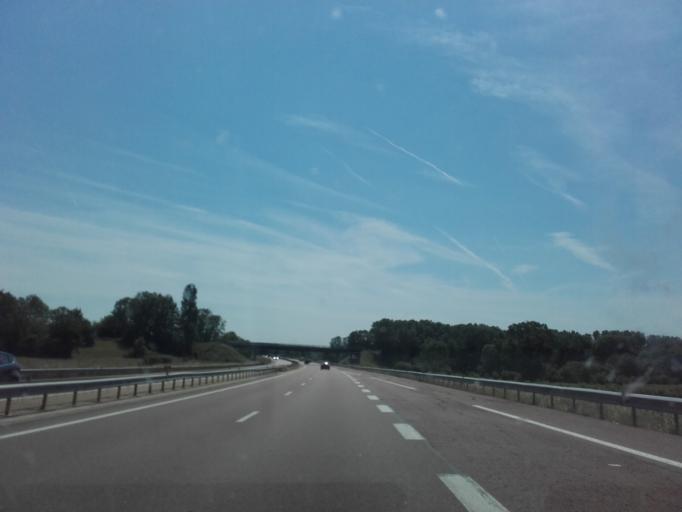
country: FR
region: Bourgogne
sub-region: Departement de l'Yonne
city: Avallon
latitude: 47.5111
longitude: 3.9981
